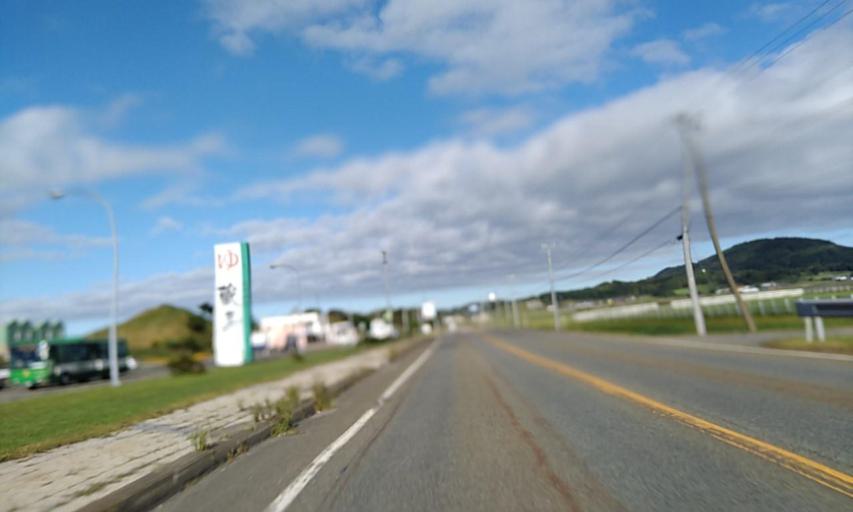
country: JP
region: Hokkaido
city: Shizunai-furukawacho
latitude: 42.2204
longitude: 142.6368
